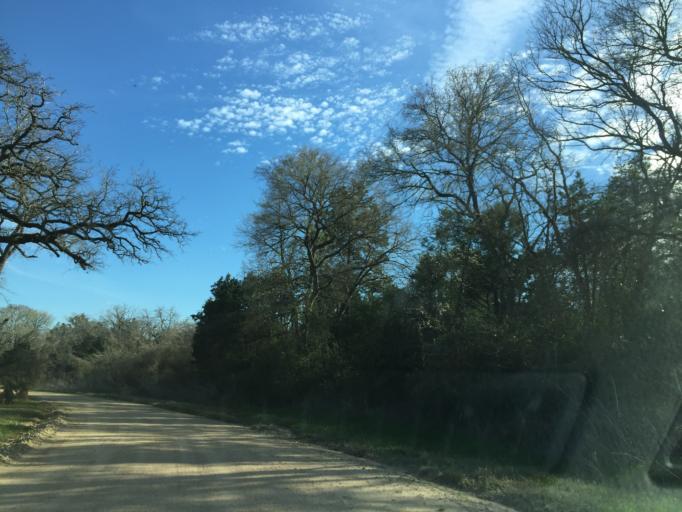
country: US
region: Texas
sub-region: Milam County
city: Thorndale
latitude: 30.4477
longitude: -97.1784
